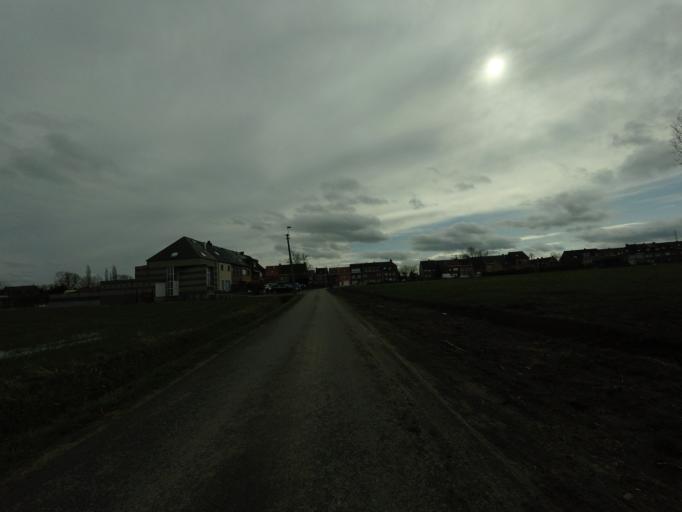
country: BE
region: Flanders
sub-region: Provincie Antwerpen
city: Schelle
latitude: 51.1270
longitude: 4.3564
